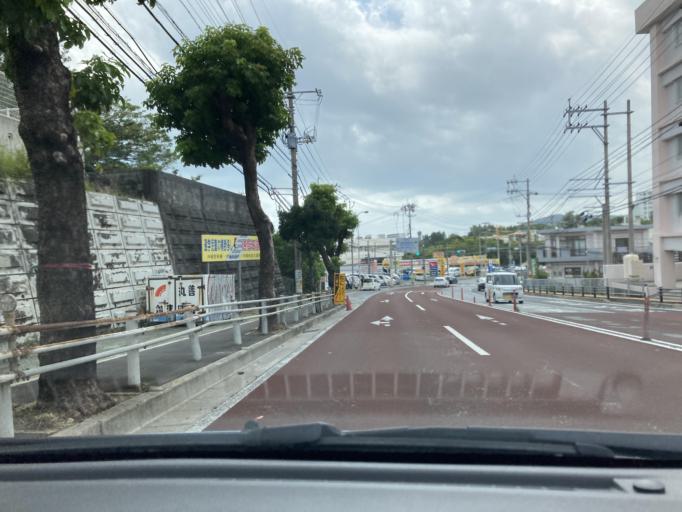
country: JP
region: Okinawa
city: Okinawa
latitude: 26.3149
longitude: 127.8191
